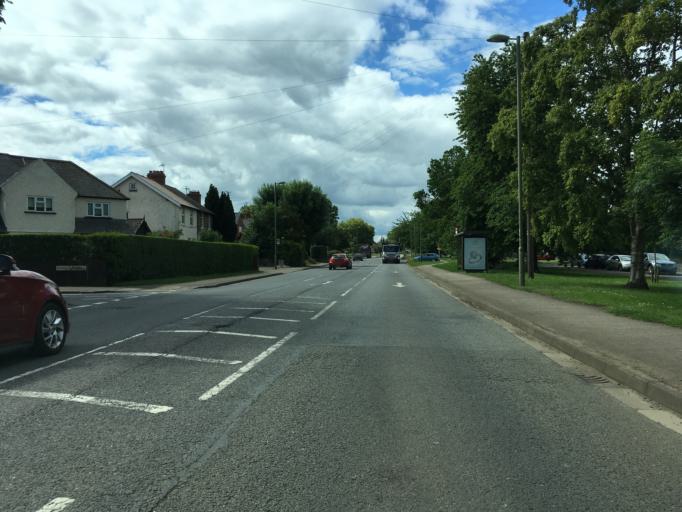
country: GB
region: England
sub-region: Oxfordshire
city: Banbury
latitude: 52.0540
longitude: -1.3450
